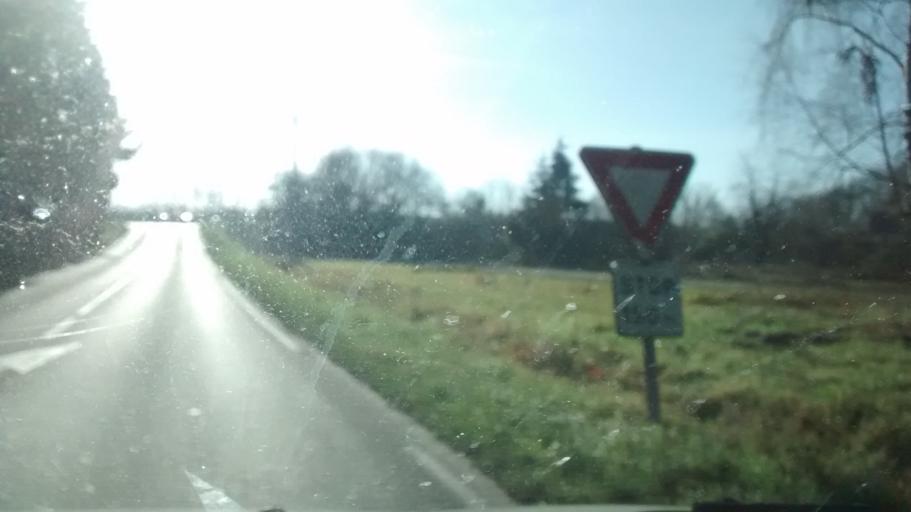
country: FR
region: Centre
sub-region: Departement d'Indre-et-Loire
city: Amboise
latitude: 47.4144
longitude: 0.9630
